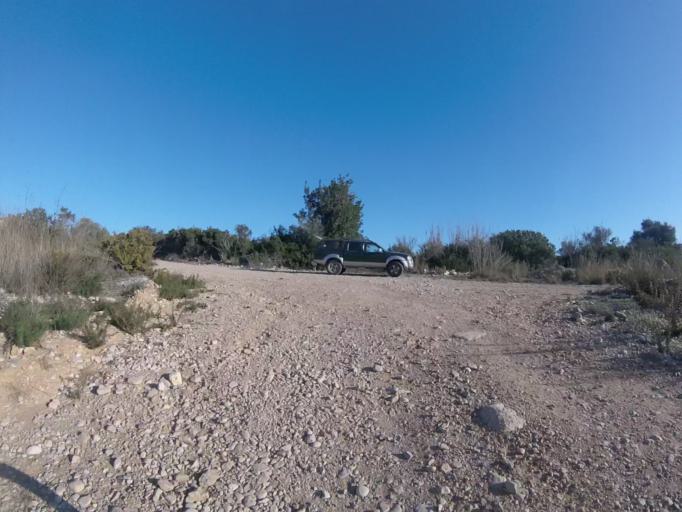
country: ES
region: Valencia
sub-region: Provincia de Castello
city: Torreblanca
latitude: 40.2640
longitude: 0.2029
